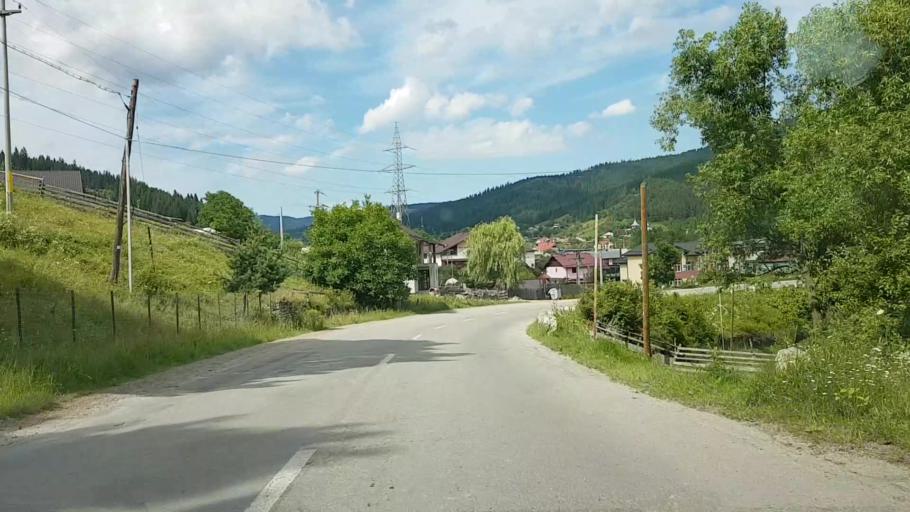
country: RO
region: Neamt
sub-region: Comuna Hangu
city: Hangu
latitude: 47.0594
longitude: 26.0327
